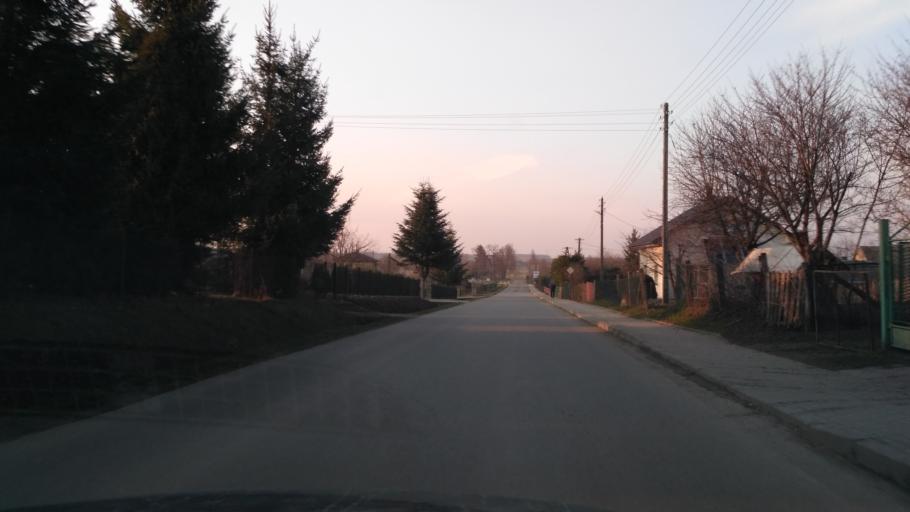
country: PL
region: Subcarpathian Voivodeship
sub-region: Powiat przeworski
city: Zarzecze
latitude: 49.9719
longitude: 22.5530
